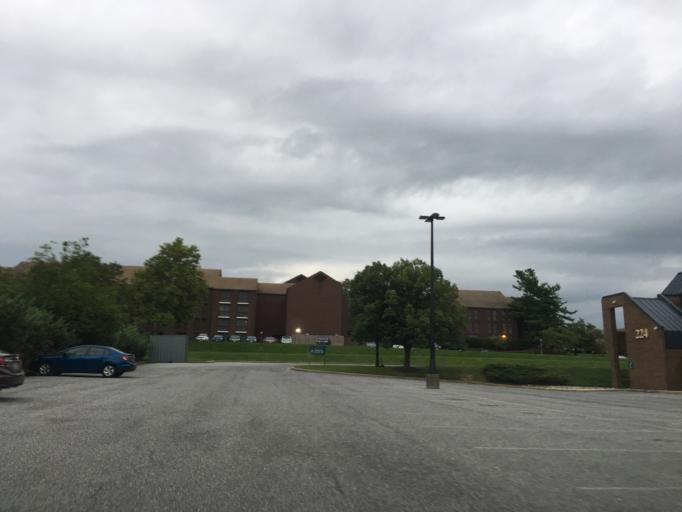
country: US
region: Maryland
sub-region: Baltimore County
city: Cockeysville
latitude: 39.4921
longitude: -76.6643
